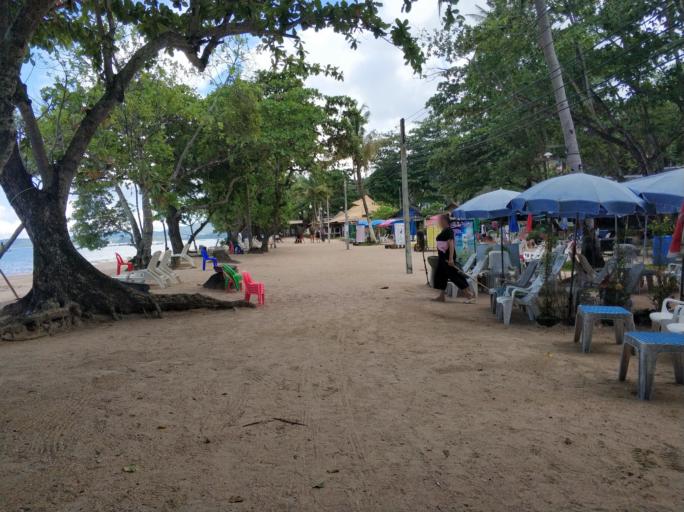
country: TH
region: Phangnga
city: Ban Ao Nang
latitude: 8.0279
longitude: 98.8257
